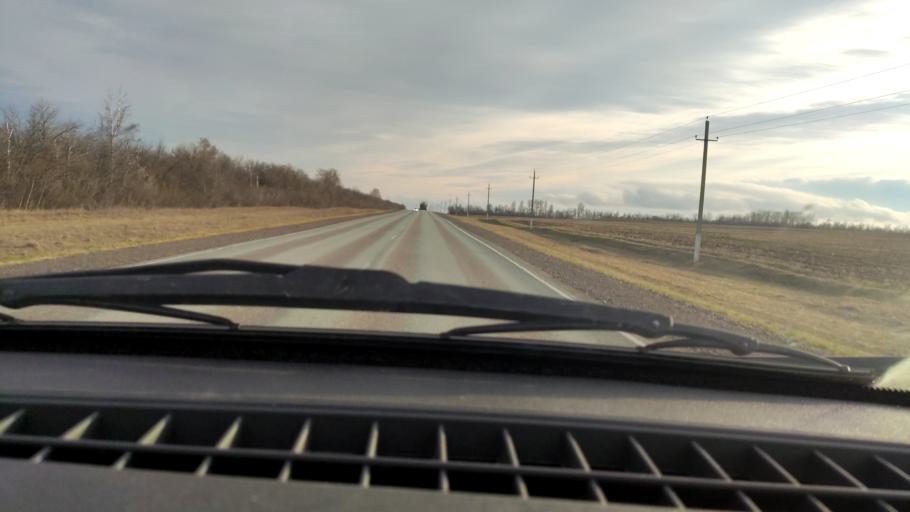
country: RU
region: Bashkortostan
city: Davlekanovo
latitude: 54.3234
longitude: 55.1586
